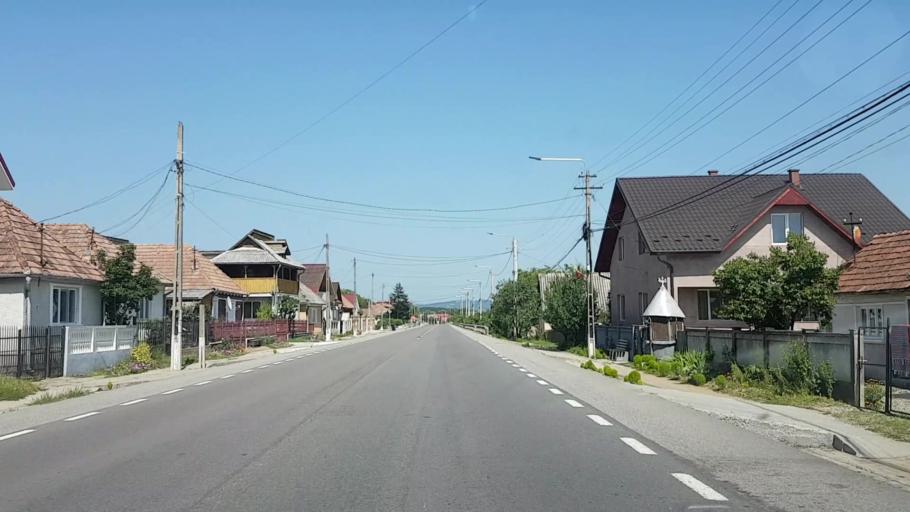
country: RO
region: Bistrita-Nasaud
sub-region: Comuna Ciceu-Mihaiesti
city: Ciceu-Mihaiesti
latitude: 47.1889
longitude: 23.9971
